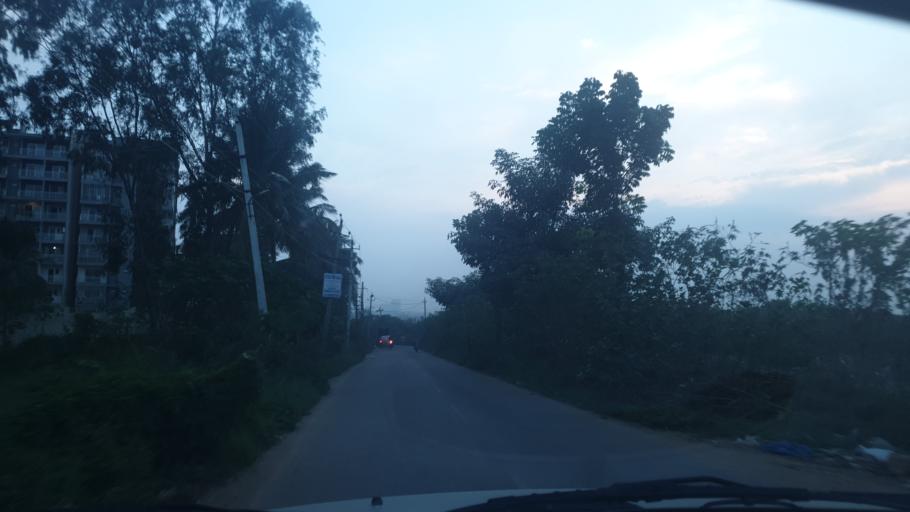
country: IN
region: Karnataka
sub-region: Bangalore Urban
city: Yelahanka
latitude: 13.0563
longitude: 77.6832
